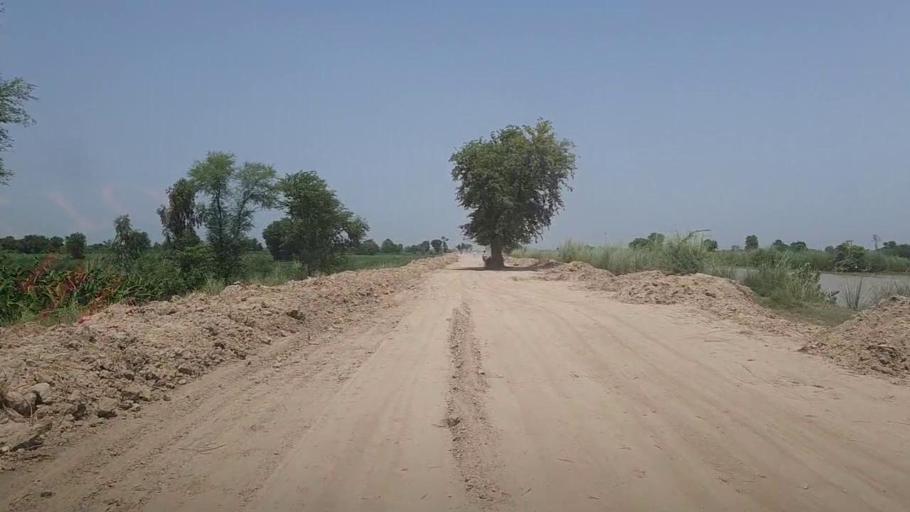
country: PK
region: Sindh
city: Pad Idan
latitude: 26.7931
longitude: 68.2753
